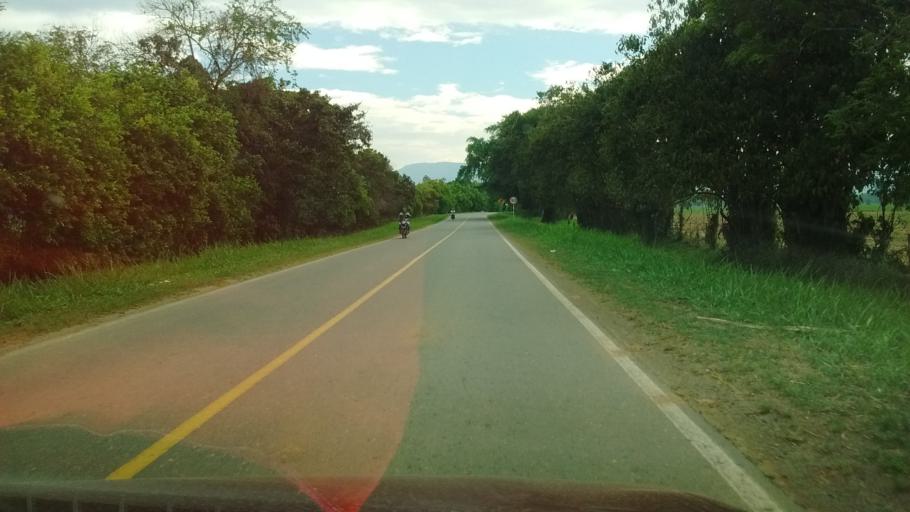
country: CO
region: Cauca
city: Caloto
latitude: 3.0449
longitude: -76.4522
